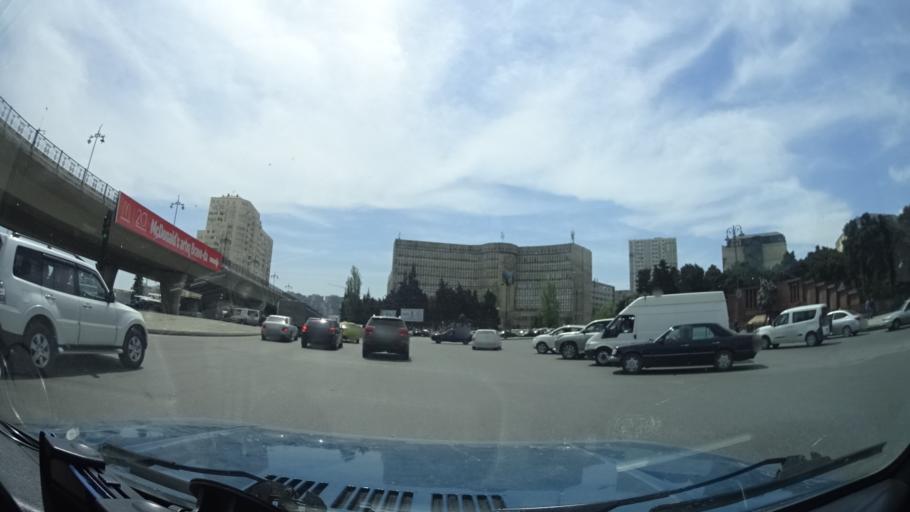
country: AZ
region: Baki
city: Khodzhi-Gasan
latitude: 40.4042
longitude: 49.8073
